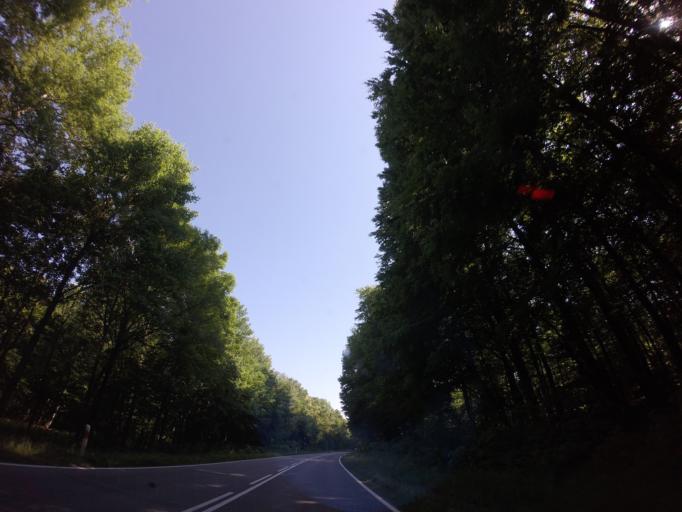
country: PL
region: West Pomeranian Voivodeship
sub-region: Powiat gryfinski
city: Stare Czarnowo
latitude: 53.3203
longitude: 14.7904
